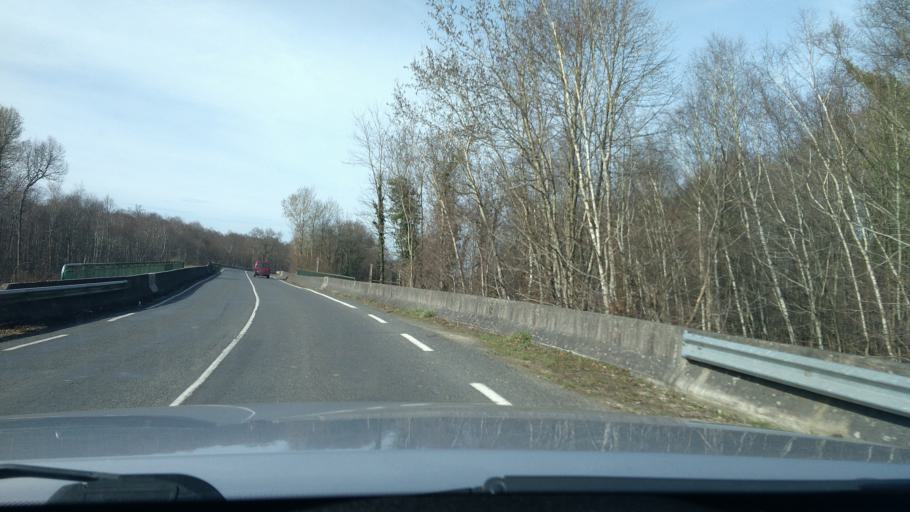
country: FR
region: Ile-de-France
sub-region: Departement de Seine-et-Marne
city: Chartrettes
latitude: 48.5005
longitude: 2.6866
